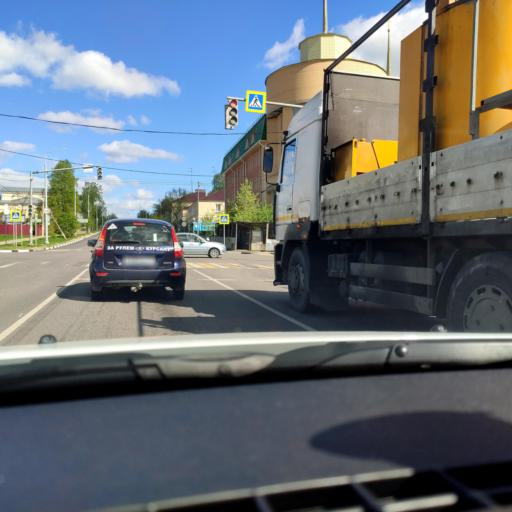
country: RU
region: Lipetsk
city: Zadonsk
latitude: 52.3934
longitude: 38.9158
